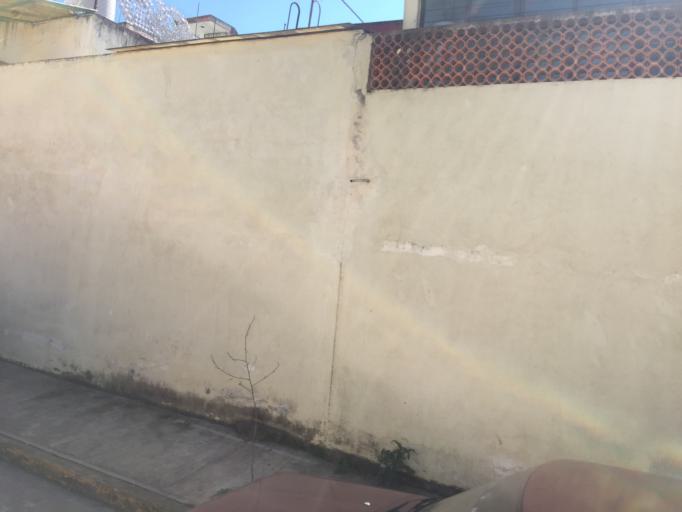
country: MX
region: Veracruz
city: El Castillo
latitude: 19.5321
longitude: -96.8862
